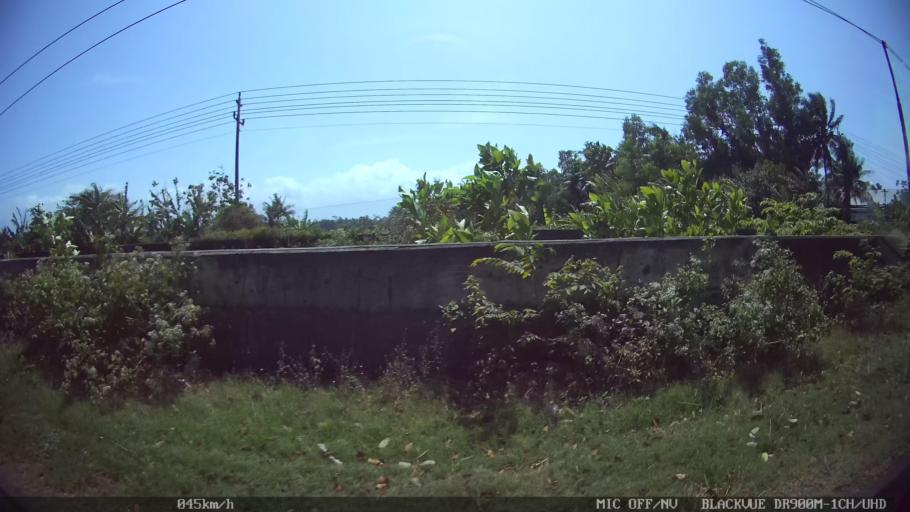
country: ID
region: Daerah Istimewa Yogyakarta
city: Srandakan
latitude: -7.9320
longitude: 110.1436
